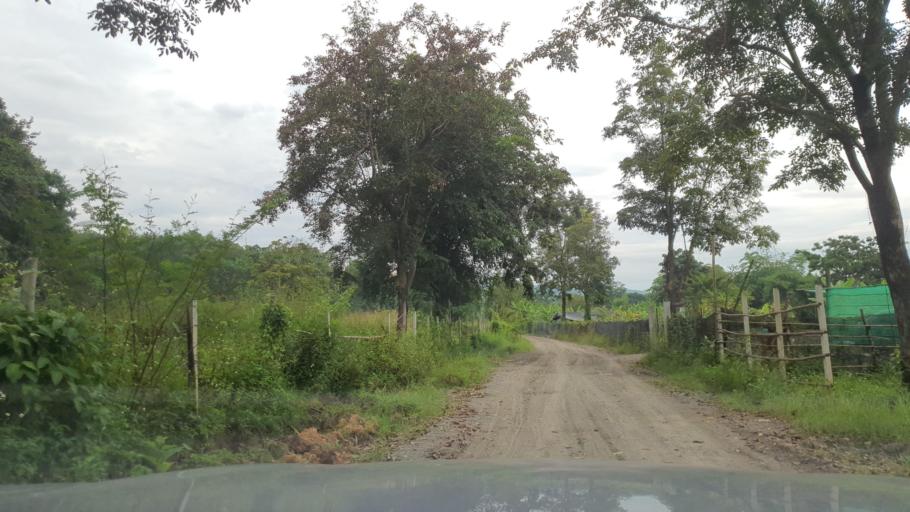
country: TH
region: Chiang Mai
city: San Sai
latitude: 18.9430
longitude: 98.9087
